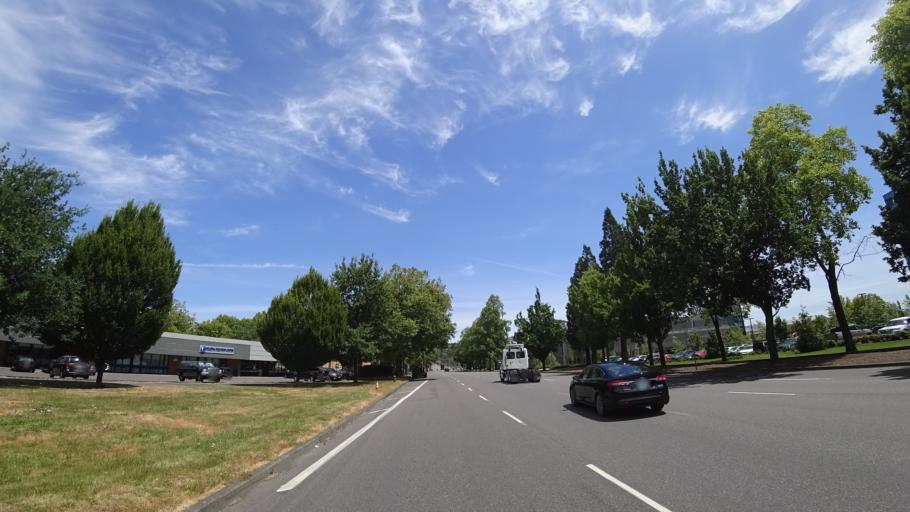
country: US
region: Oregon
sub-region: Multnomah County
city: Portland
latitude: 45.5566
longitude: -122.7033
